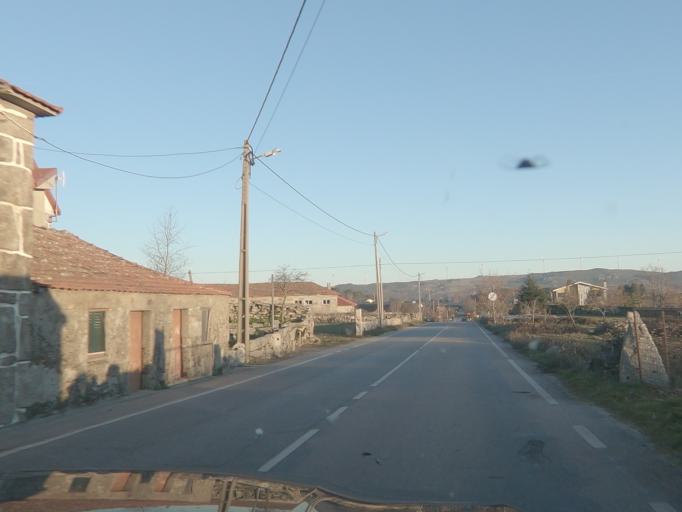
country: PT
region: Vila Real
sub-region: Vila Pouca de Aguiar
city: Vila Pouca de Aguiar
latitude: 41.4966
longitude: -7.6792
